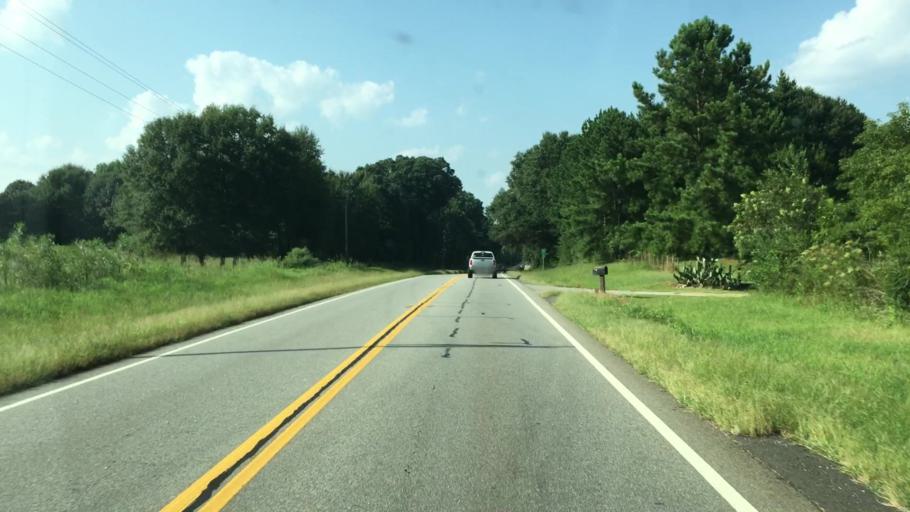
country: US
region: Georgia
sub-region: Walton County
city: Monroe
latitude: 33.8826
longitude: -83.7211
